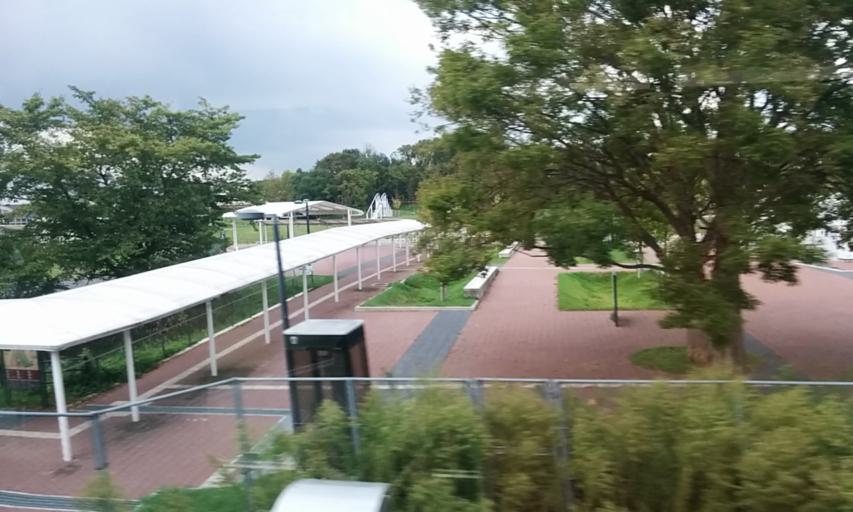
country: JP
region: Nara
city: Tawaramoto
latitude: 34.5987
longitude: 135.7851
